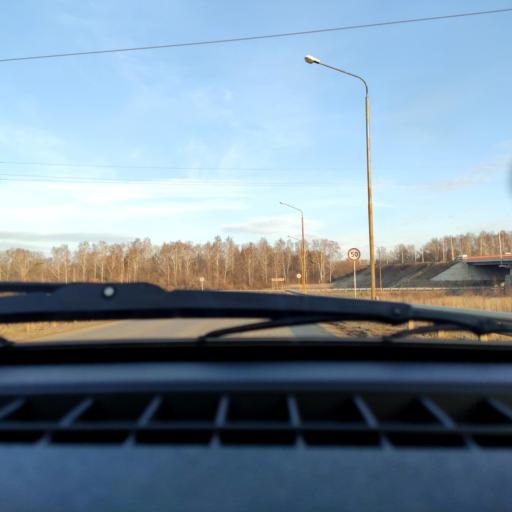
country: RU
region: Bashkortostan
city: Iglino
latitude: 54.7710
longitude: 56.2578
